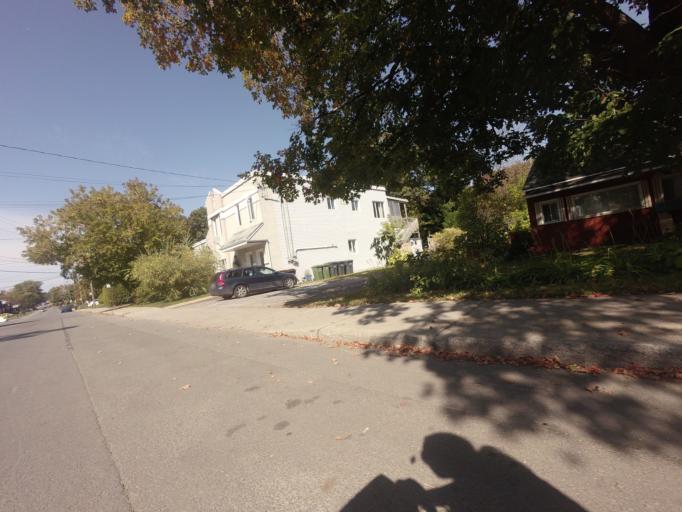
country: CA
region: Quebec
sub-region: Laurentides
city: Deux-Montagnes
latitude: 45.5394
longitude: -73.8886
